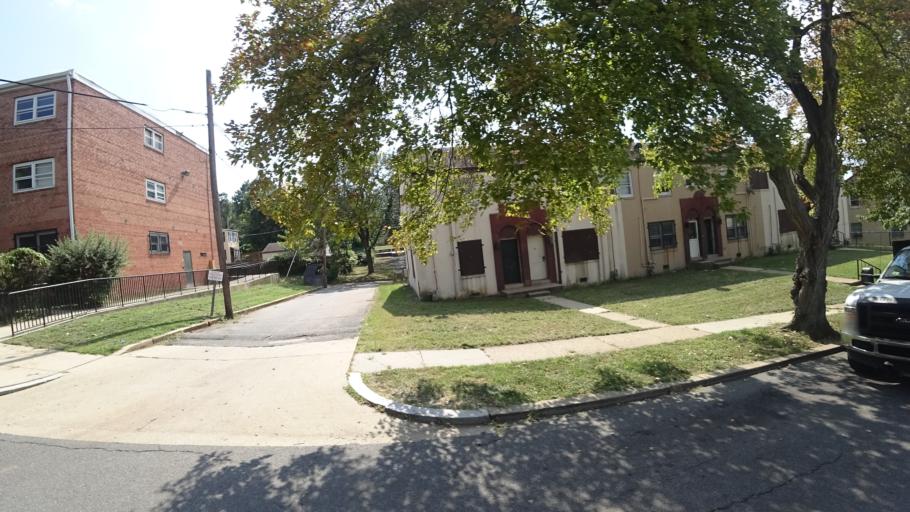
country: US
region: Maryland
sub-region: Prince George's County
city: Glassmanor
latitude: 38.8591
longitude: -76.9978
